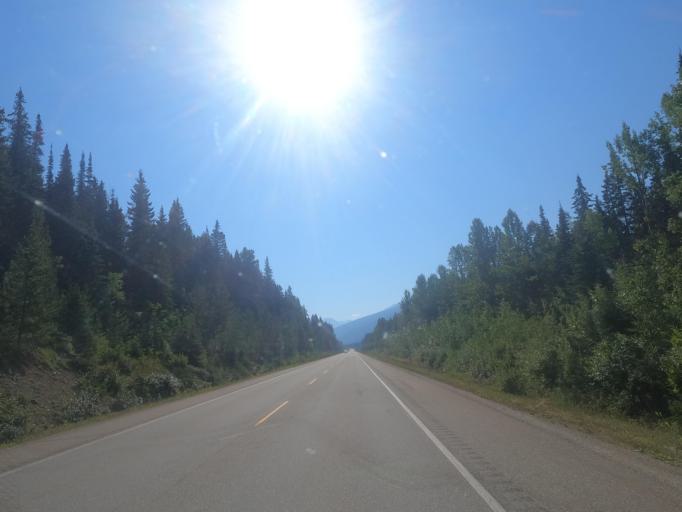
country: CA
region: Alberta
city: Jasper Park Lodge
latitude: 52.9032
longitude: -118.7653
